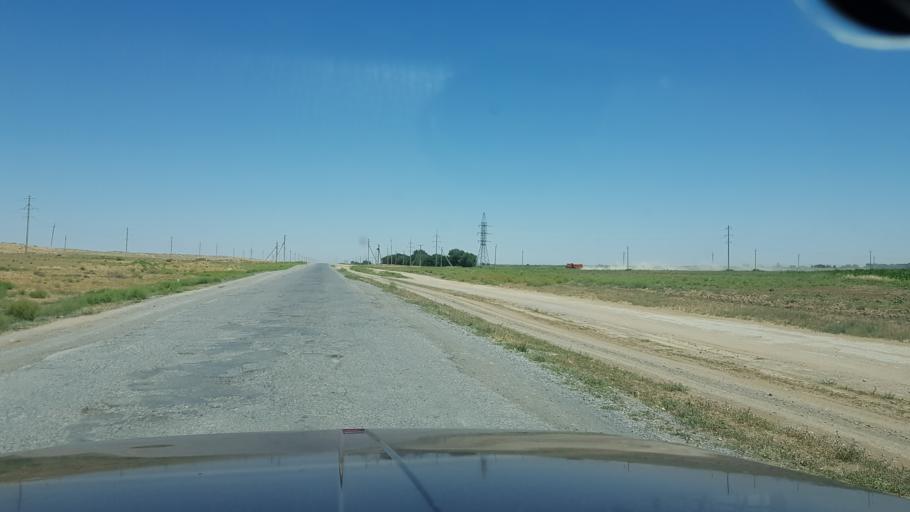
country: TM
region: Ahal
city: Annau
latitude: 37.8652
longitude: 58.7137
